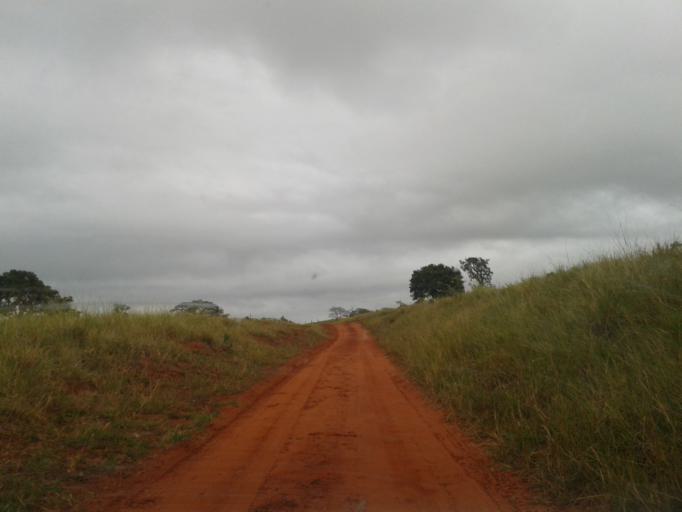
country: BR
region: Minas Gerais
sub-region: Campina Verde
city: Campina Verde
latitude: -19.4095
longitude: -49.6477
